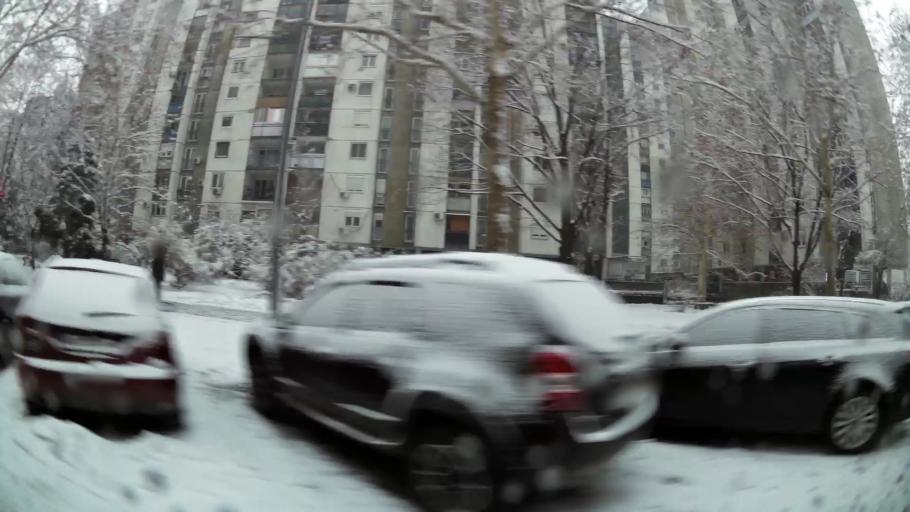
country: RS
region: Central Serbia
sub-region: Belgrade
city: Cukarica
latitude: 44.8014
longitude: 20.3749
